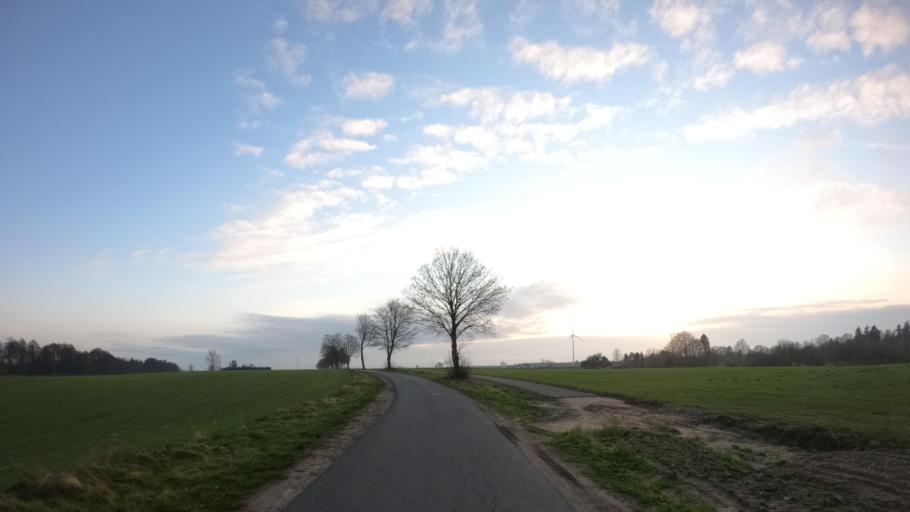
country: PL
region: West Pomeranian Voivodeship
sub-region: Powiat bialogardzki
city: Karlino
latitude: 54.1027
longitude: 15.8854
